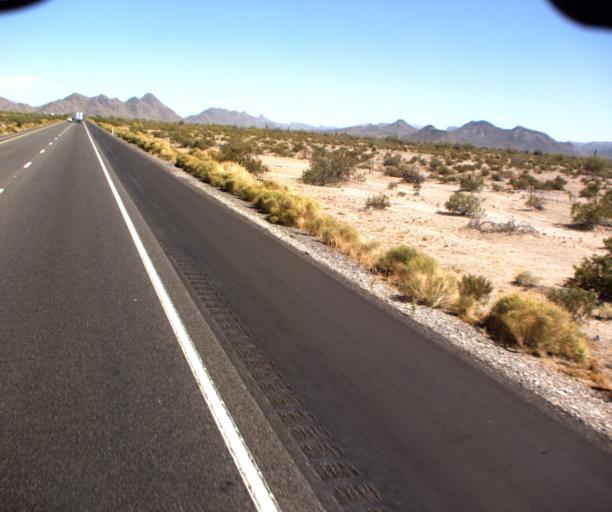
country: US
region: Arizona
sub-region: Maricopa County
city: Gila Bend
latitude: 32.9083
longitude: -112.5948
